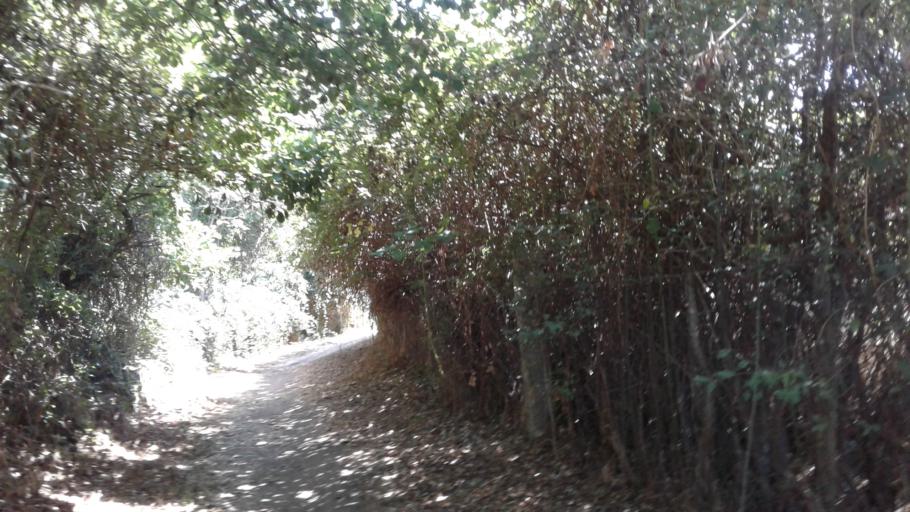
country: IT
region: Sardinia
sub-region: Provincia di Olbia-Tempio
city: Calangianus
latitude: 40.9086
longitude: 9.1723
